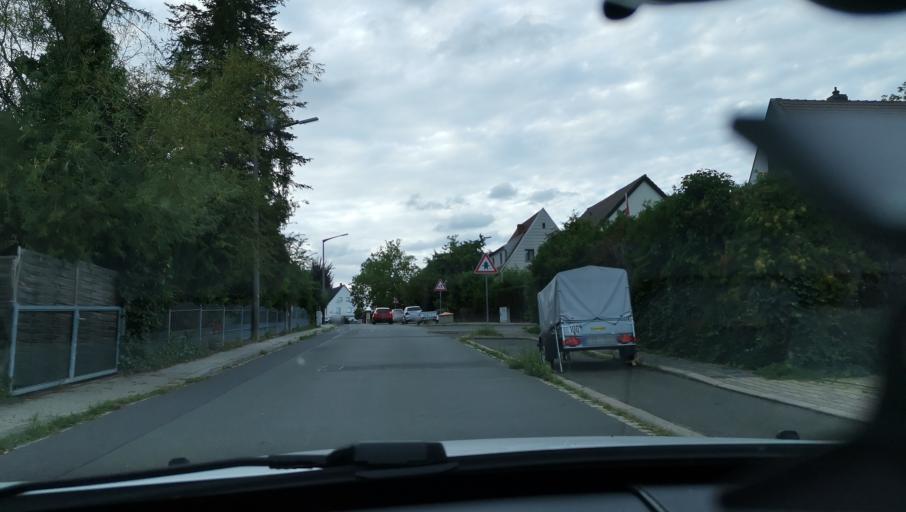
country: DE
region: Bavaria
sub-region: Regierungsbezirk Mittelfranken
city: Zirndorf
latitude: 49.4451
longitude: 10.9469
